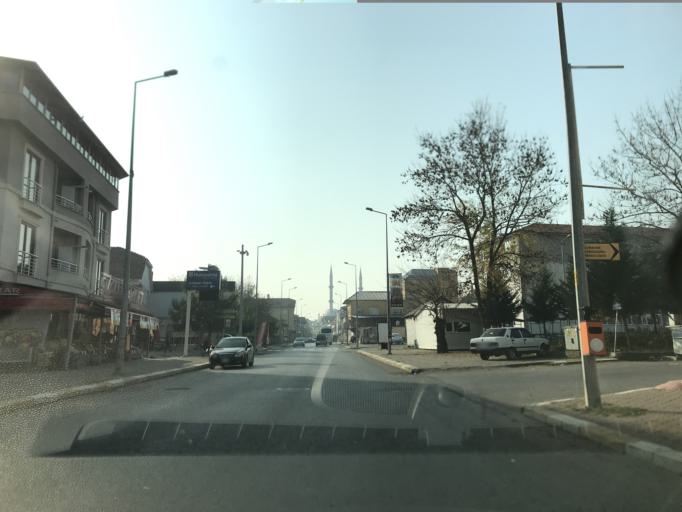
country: TR
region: Duzce
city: Cumayeri
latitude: 40.8799
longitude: 30.9508
